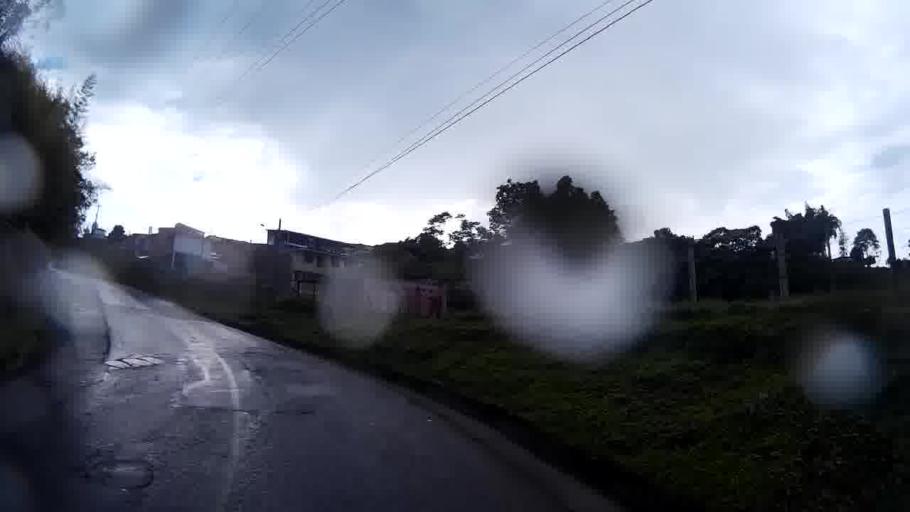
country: CO
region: Quindio
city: Filandia
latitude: 4.6766
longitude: -75.6541
